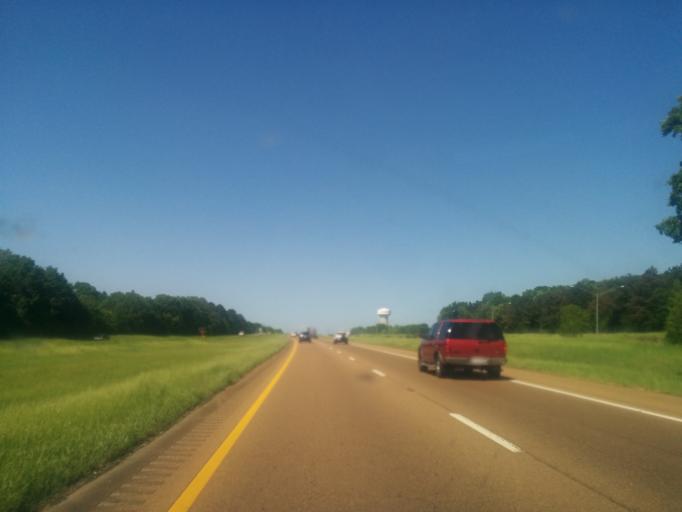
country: US
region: Mississippi
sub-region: Madison County
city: Canton
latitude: 32.5553
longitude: -90.0850
